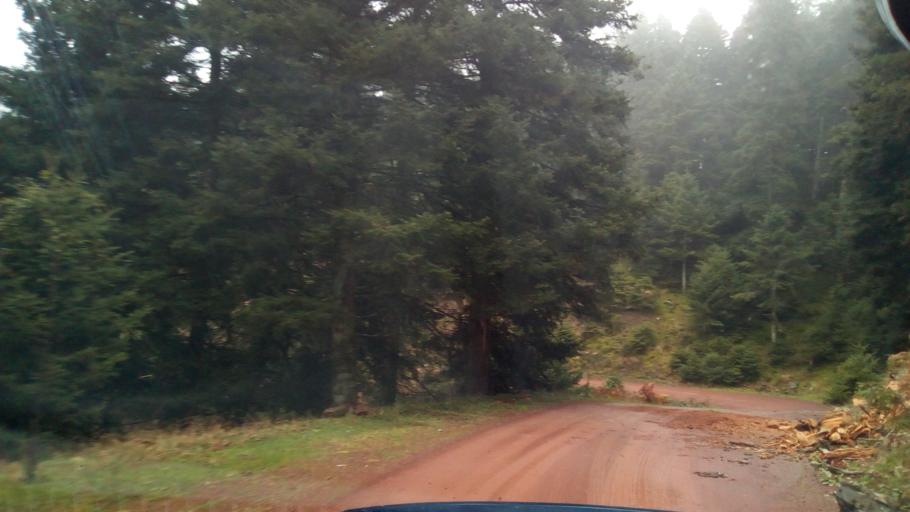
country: GR
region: West Greece
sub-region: Nomos Aitolias kai Akarnanias
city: Nafpaktos
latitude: 38.5393
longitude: 21.8619
